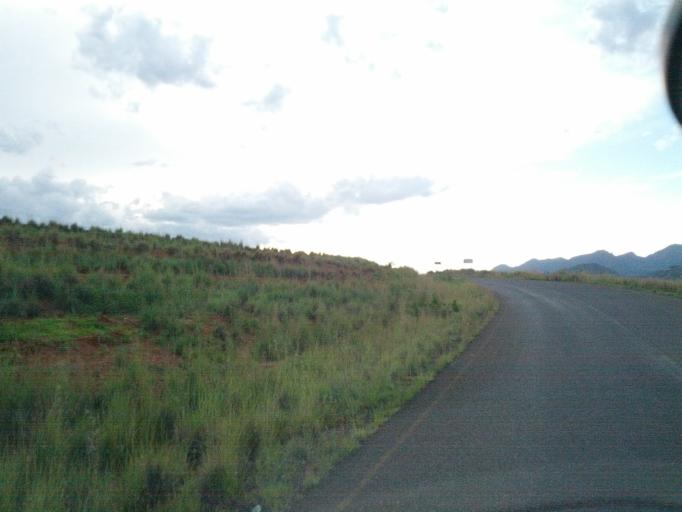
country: LS
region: Qacha's Nek
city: Qacha's Nek
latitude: -30.0639
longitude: 28.6135
